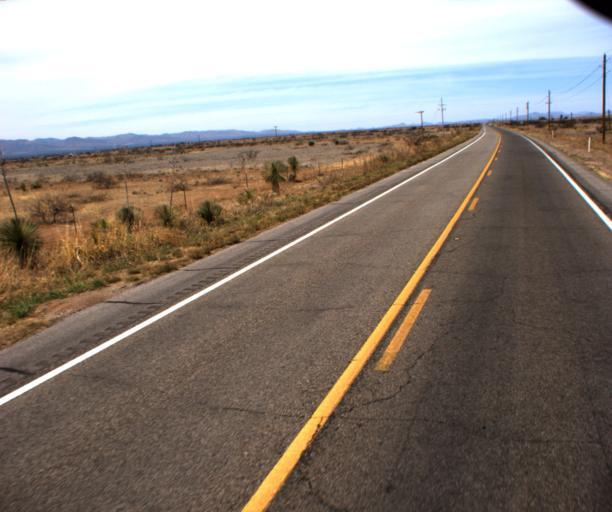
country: US
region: Arizona
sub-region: Cochise County
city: Pirtleville
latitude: 31.4357
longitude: -109.5900
